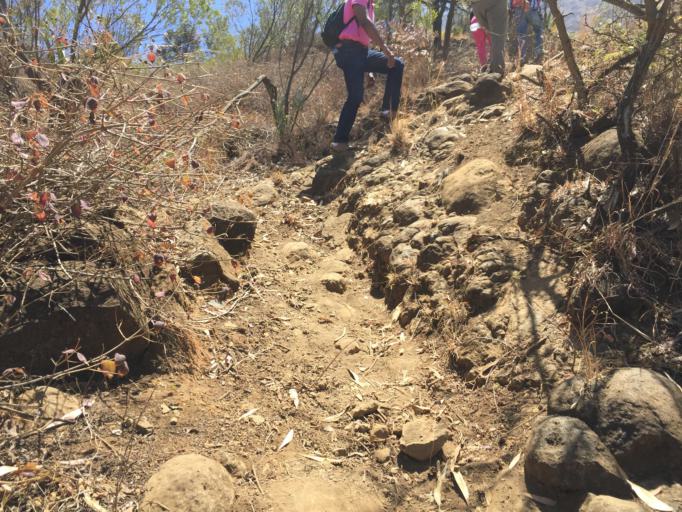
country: CV
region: Mosteiros
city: Porto dos Mosteiros
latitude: 15.0087
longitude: -24.3824
